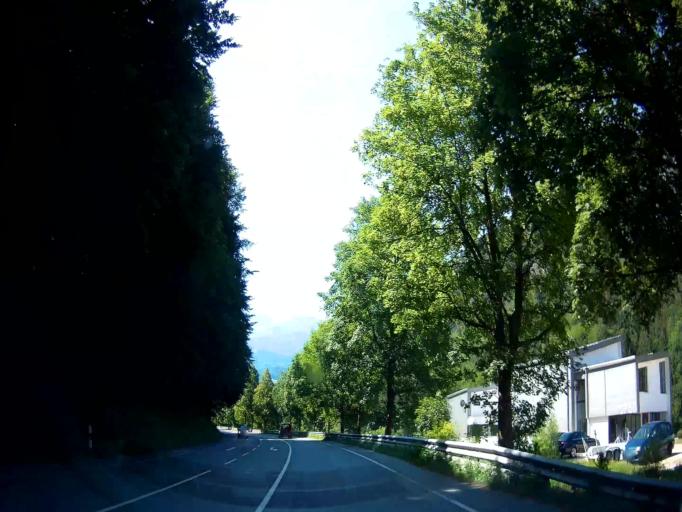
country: DE
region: Bavaria
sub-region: Upper Bavaria
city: Marktschellenberg
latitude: 47.6649
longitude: 13.0350
